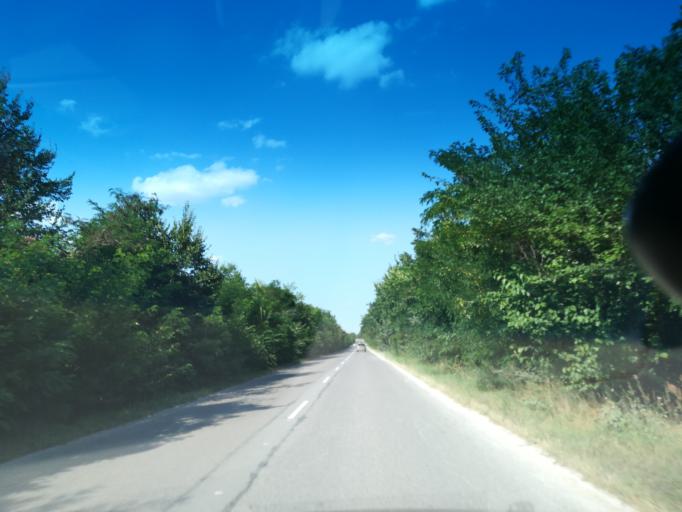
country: BG
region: Stara Zagora
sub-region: Obshtina Chirpan
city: Chirpan
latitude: 42.2433
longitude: 25.4067
